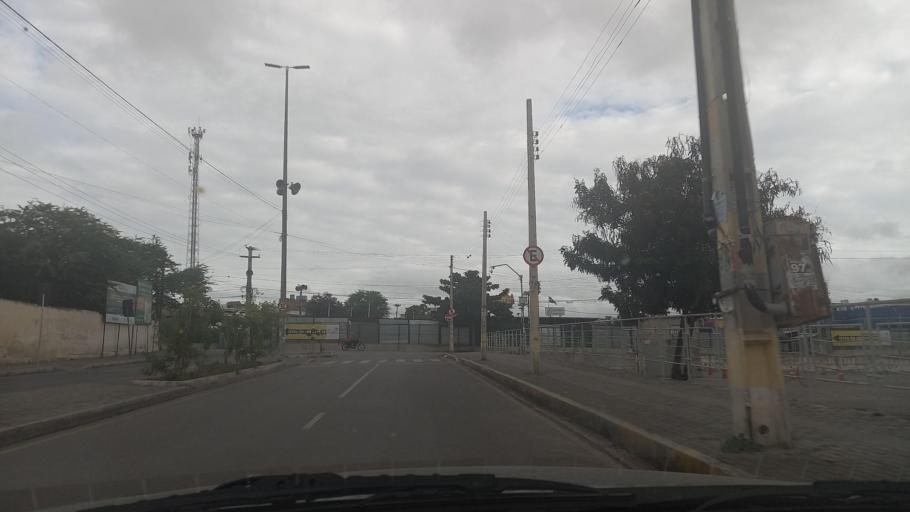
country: BR
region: Pernambuco
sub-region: Caruaru
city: Caruaru
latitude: -8.2922
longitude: -35.9707
